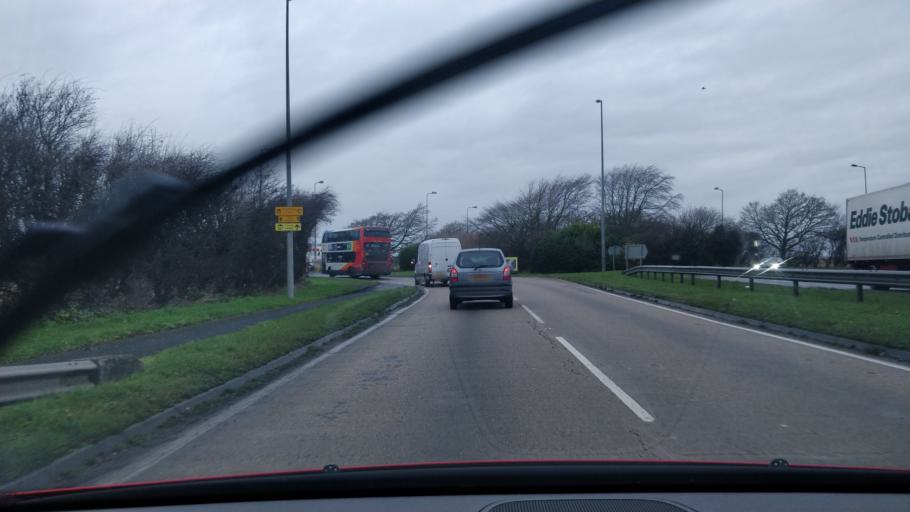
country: GB
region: England
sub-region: Sefton
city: Hightown
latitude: 53.5436
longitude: -3.0483
